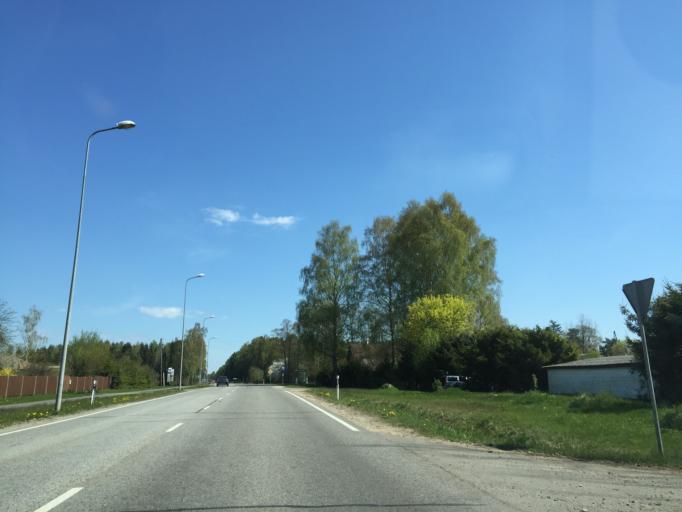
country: LV
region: Saulkrastu
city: Saulkrasti
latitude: 57.3204
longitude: 24.4239
